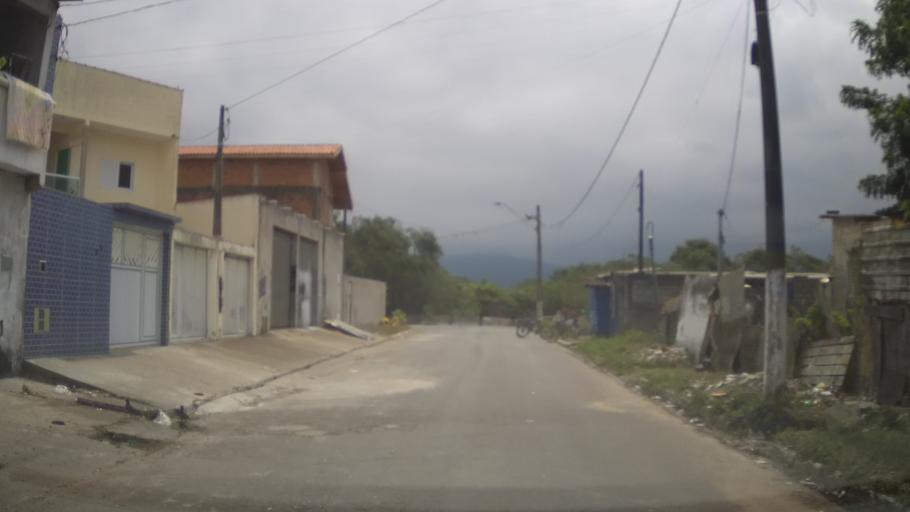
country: BR
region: Sao Paulo
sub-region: Praia Grande
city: Praia Grande
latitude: -23.9956
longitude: -46.4488
